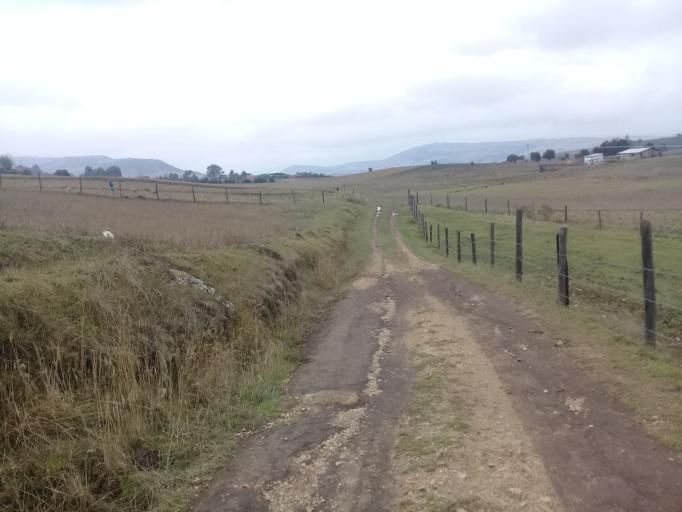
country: CO
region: Boyaca
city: Siachoque
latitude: 5.5637
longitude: -73.2765
